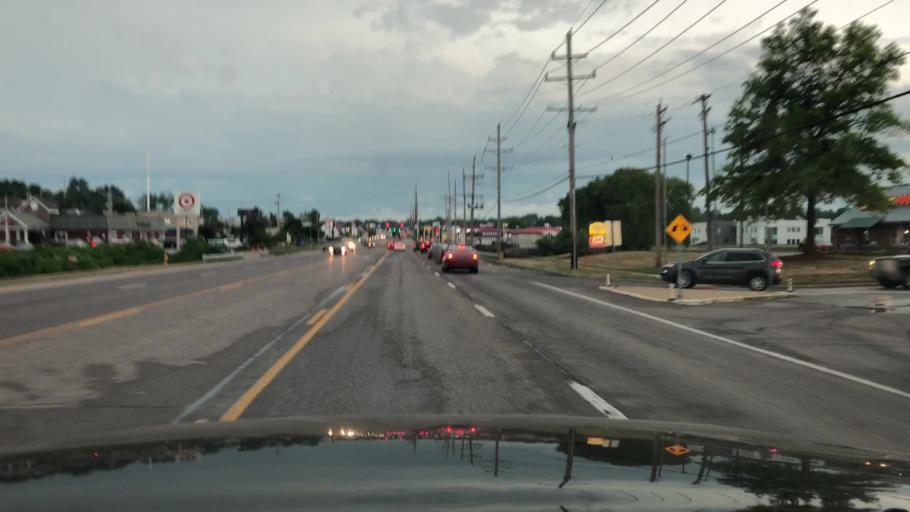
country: US
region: Missouri
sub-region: Saint Louis County
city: Bridgeton
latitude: 38.7527
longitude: -90.4281
